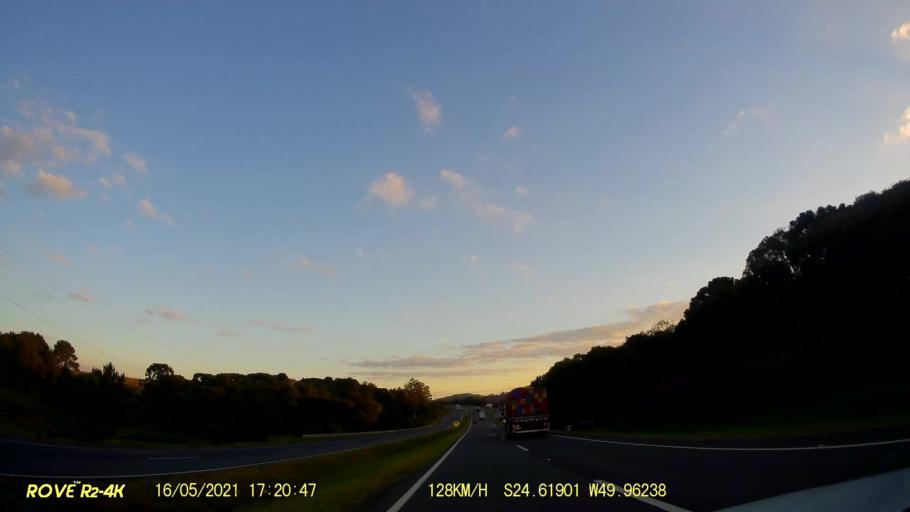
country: BR
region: Parana
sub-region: Pirai Do Sul
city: Pirai do Sul
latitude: -24.6194
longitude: -49.9626
